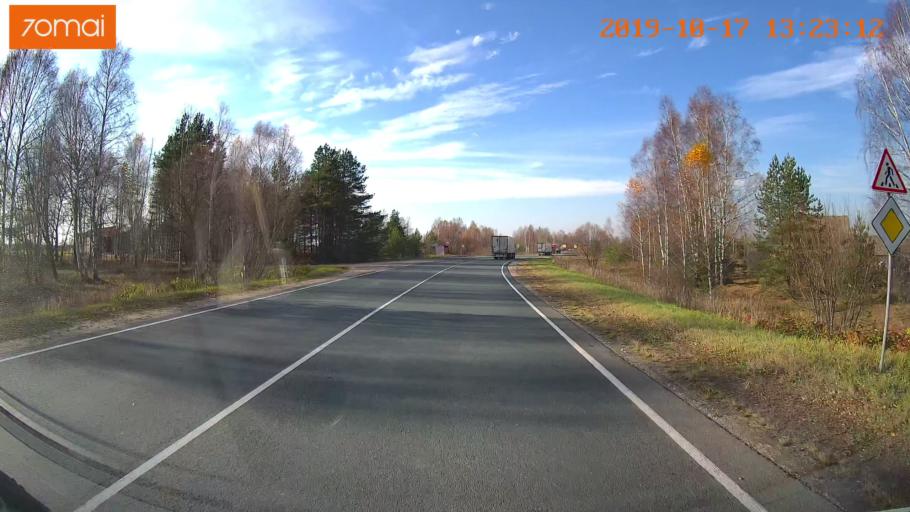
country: RU
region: Rjazan
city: Gus'-Zheleznyy
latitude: 55.0882
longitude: 40.9837
